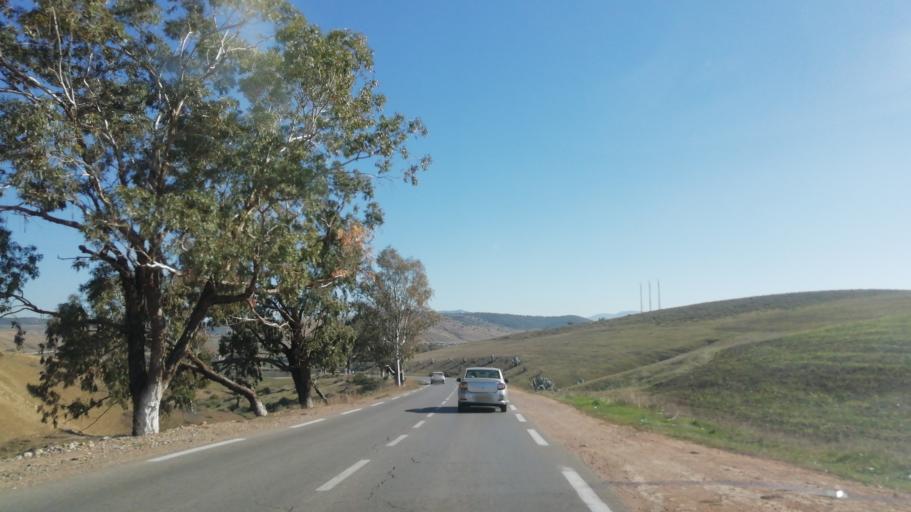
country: DZ
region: Tlemcen
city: Nedroma
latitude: 34.8284
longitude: -1.6626
